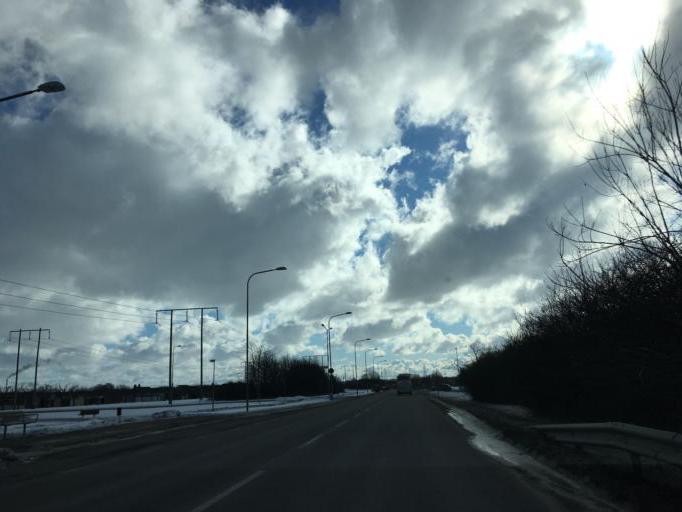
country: SE
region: Vaestmanland
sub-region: Vasteras
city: Vasteras
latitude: 59.6007
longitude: 16.4608
